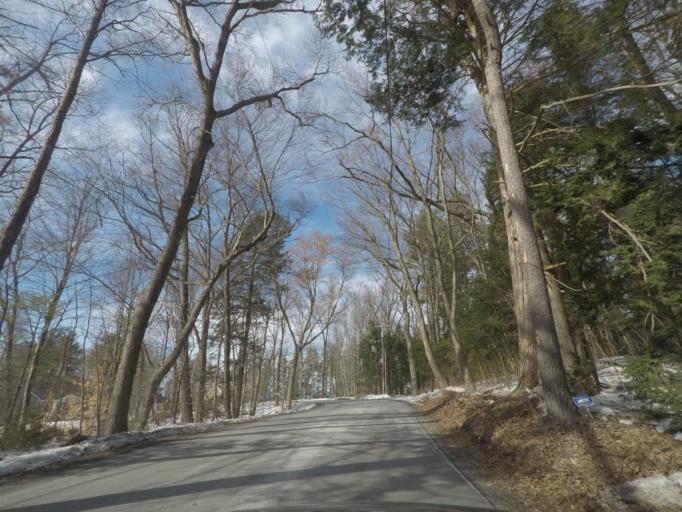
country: US
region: New York
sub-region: Albany County
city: Voorheesville
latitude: 42.6580
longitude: -73.9556
